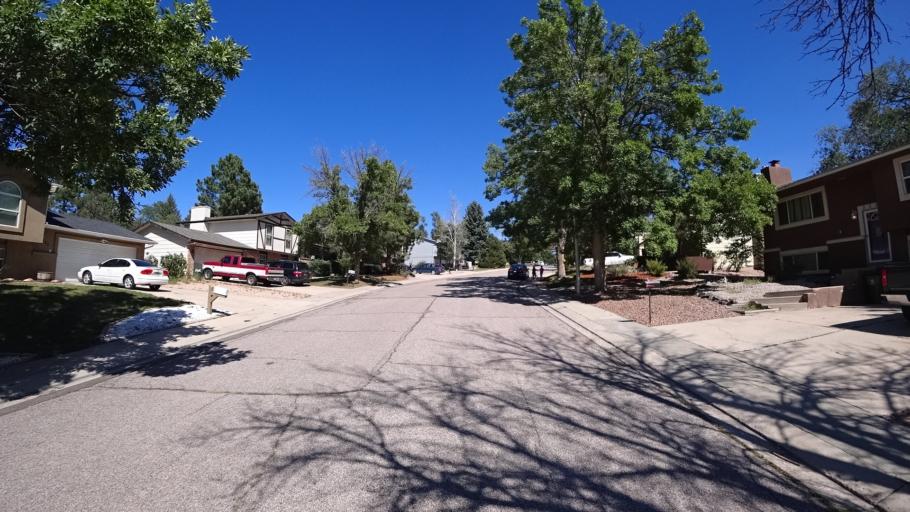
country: US
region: Colorado
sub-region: El Paso County
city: Cimarron Hills
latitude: 38.8782
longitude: -104.7324
